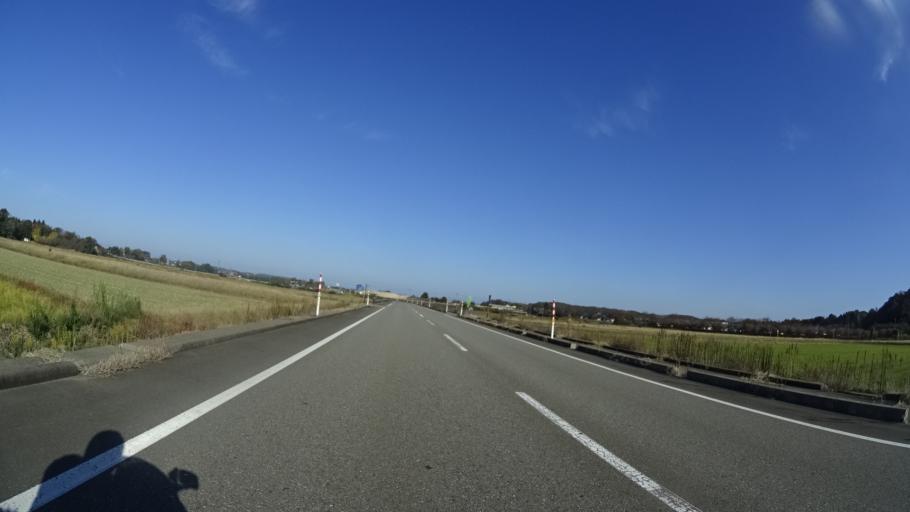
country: JP
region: Ishikawa
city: Komatsu
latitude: 36.2972
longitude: 136.3882
